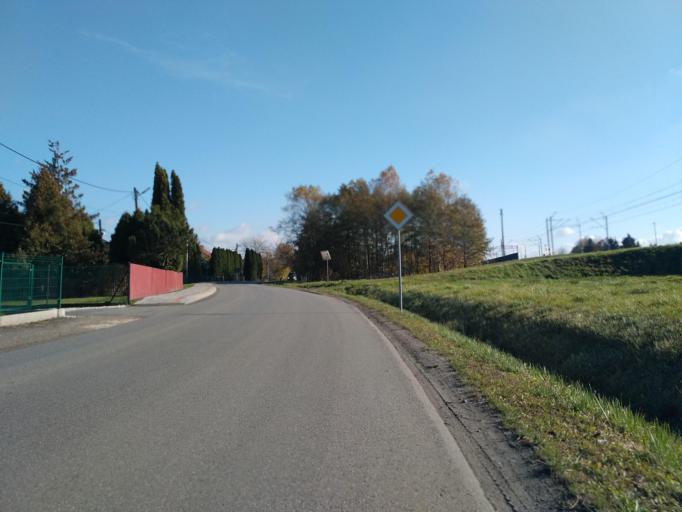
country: PL
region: Subcarpathian Voivodeship
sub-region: Powiat rzeszowski
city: Trzciana
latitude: 50.0789
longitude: 21.8334
